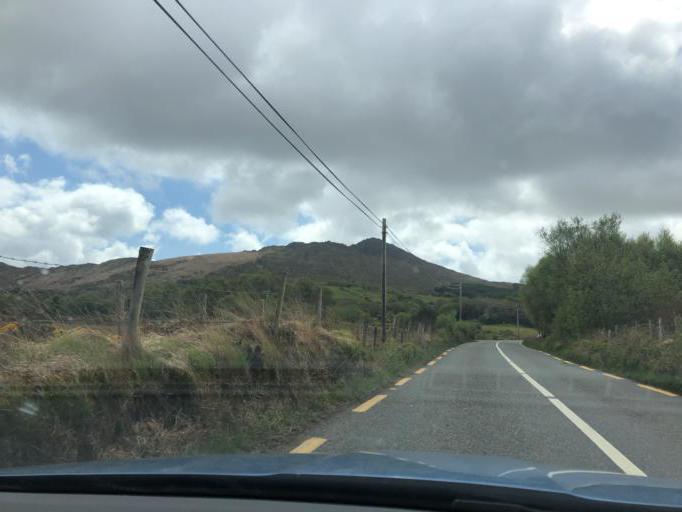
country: IE
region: Munster
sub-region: Ciarrai
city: Killorglin
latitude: 51.8302
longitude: -9.9336
